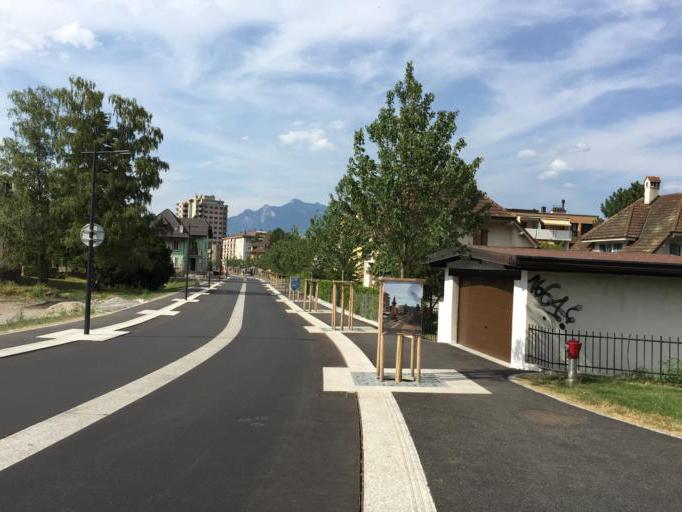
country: CH
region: Valais
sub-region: Monthey District
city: Monthey
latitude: 46.2501
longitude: 6.9505
